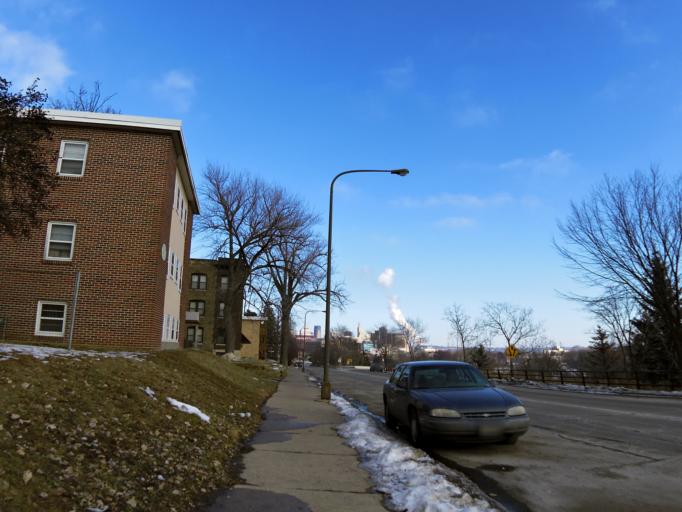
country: US
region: Minnesota
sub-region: Ramsey County
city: Saint Paul
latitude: 44.9398
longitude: -93.1177
